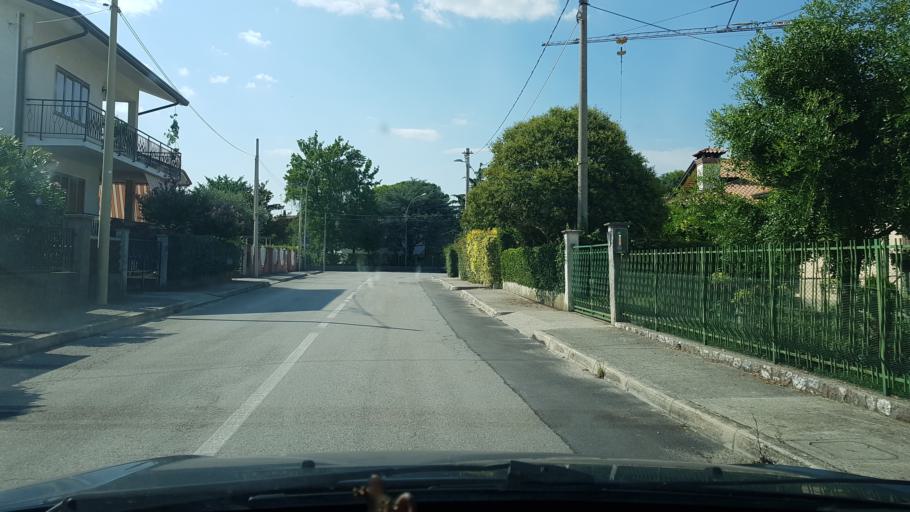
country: IT
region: Friuli Venezia Giulia
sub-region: Provincia di Gorizia
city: Staranzano
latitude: 45.7934
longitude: 13.5042
